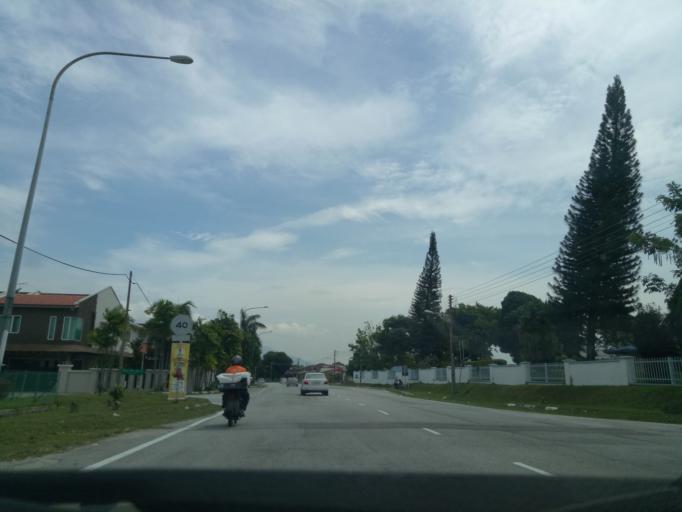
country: MY
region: Perak
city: Ipoh
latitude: 4.6092
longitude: 101.1159
